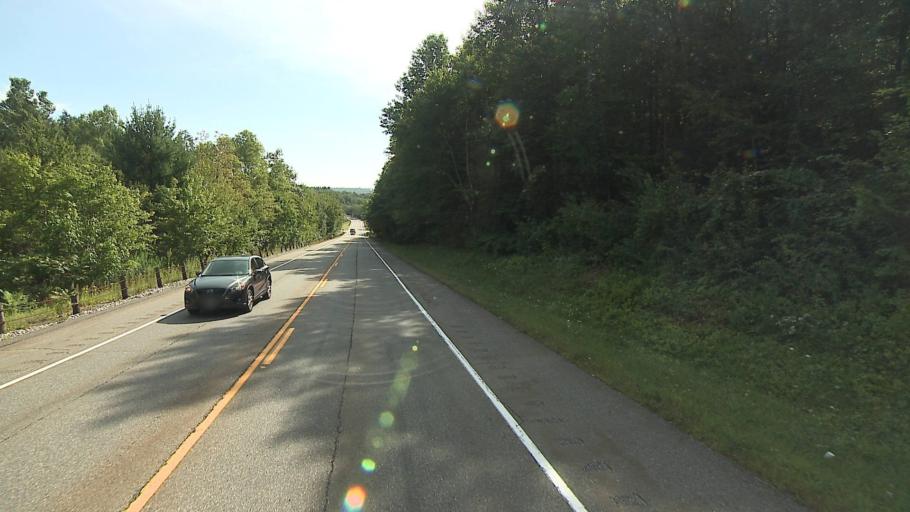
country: US
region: Connecticut
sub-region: Litchfield County
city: Torrington
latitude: 41.7614
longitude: -73.1420
